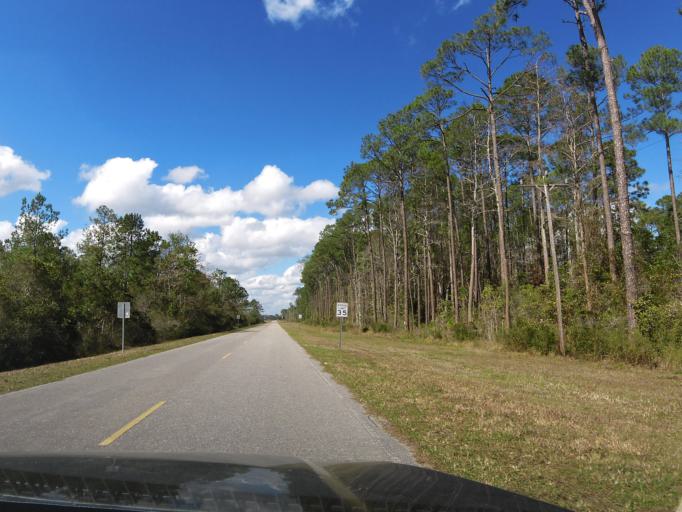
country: US
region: Florida
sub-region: Clay County
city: Green Cove Springs
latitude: 29.8680
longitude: -81.6724
